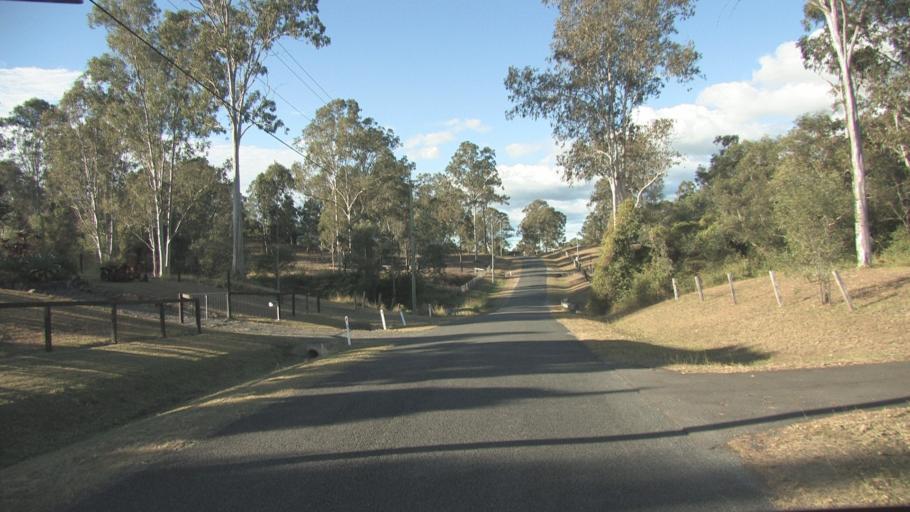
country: AU
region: Queensland
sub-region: Logan
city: Cedar Vale
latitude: -27.9292
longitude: 153.0674
